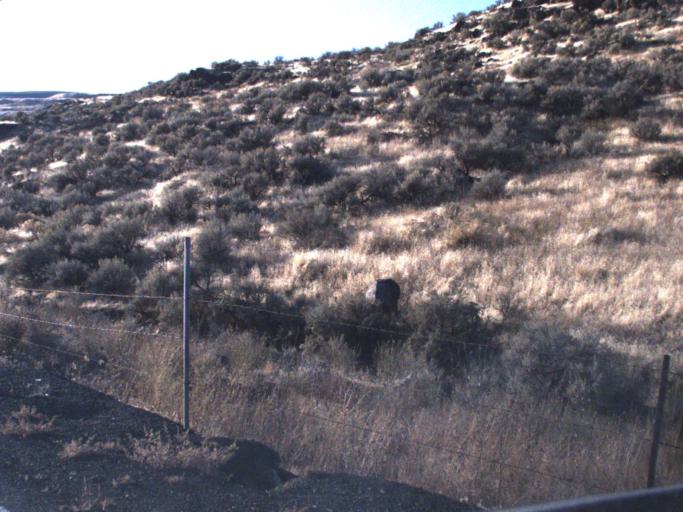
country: US
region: Washington
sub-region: Adams County
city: Ritzville
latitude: 46.6986
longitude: -118.3992
